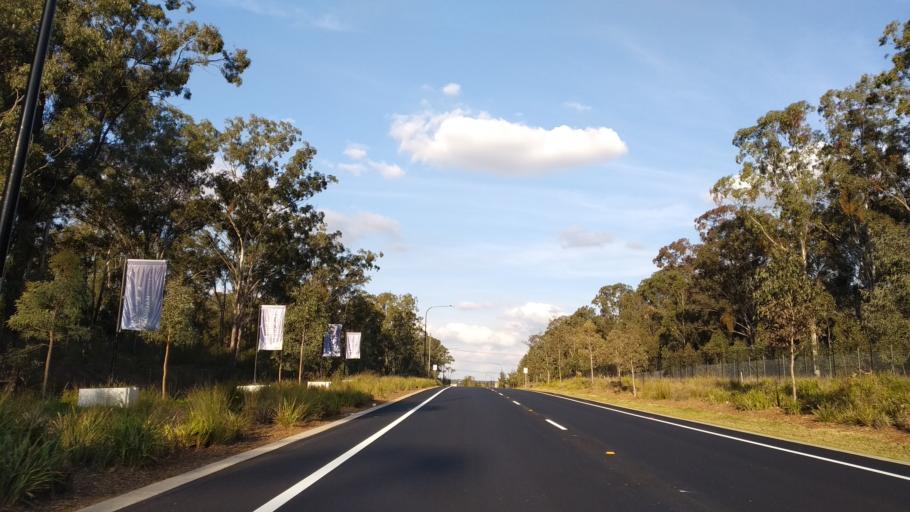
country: AU
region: New South Wales
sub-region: Penrith Municipality
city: Werrington County
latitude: -33.7318
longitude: 150.7449
